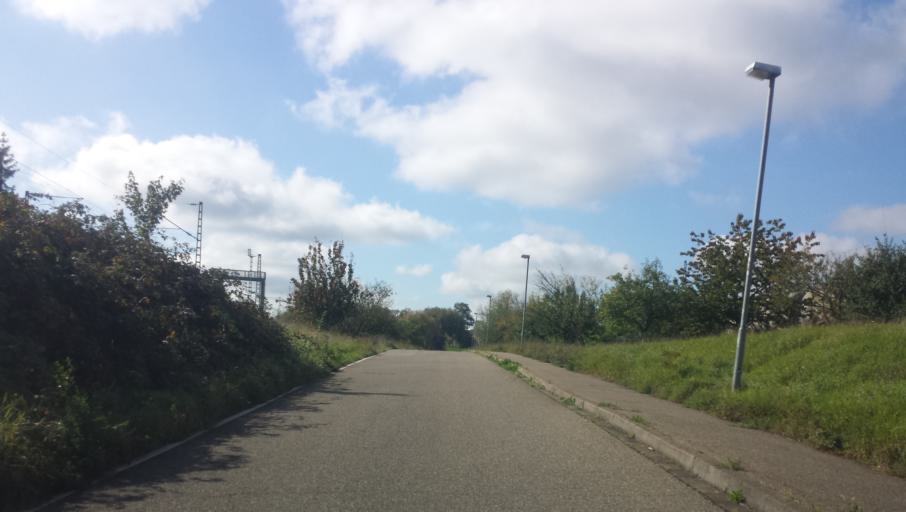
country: DE
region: Baden-Wuerttemberg
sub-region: Karlsruhe Region
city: Waghausel
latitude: 49.2510
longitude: 8.5102
